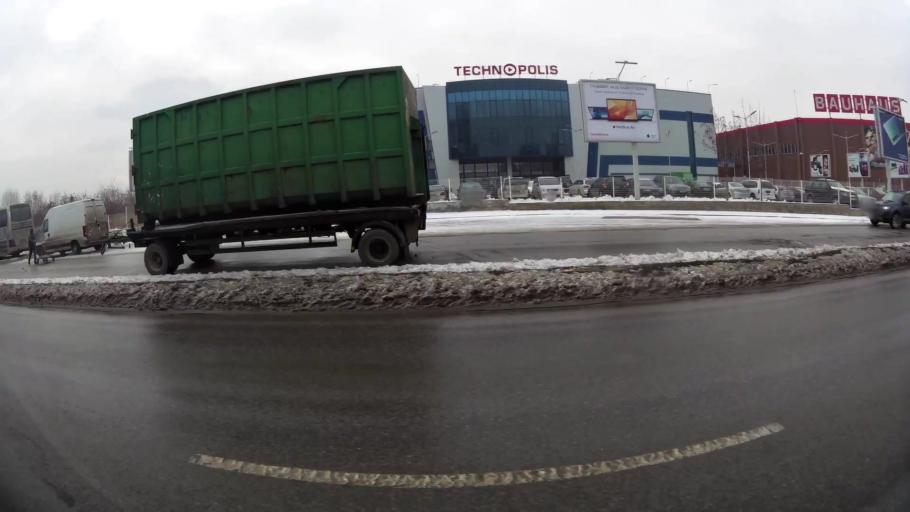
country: BG
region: Sofia-Capital
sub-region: Stolichna Obshtina
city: Sofia
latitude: 42.7177
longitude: 23.3183
